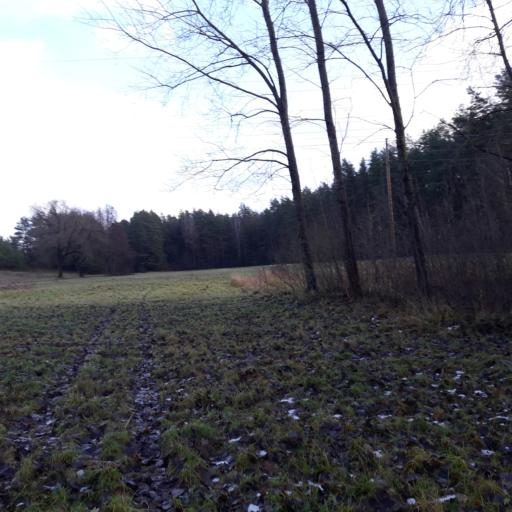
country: LV
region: Valmieras Rajons
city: Valmiera
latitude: 57.5463
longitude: 25.4620
